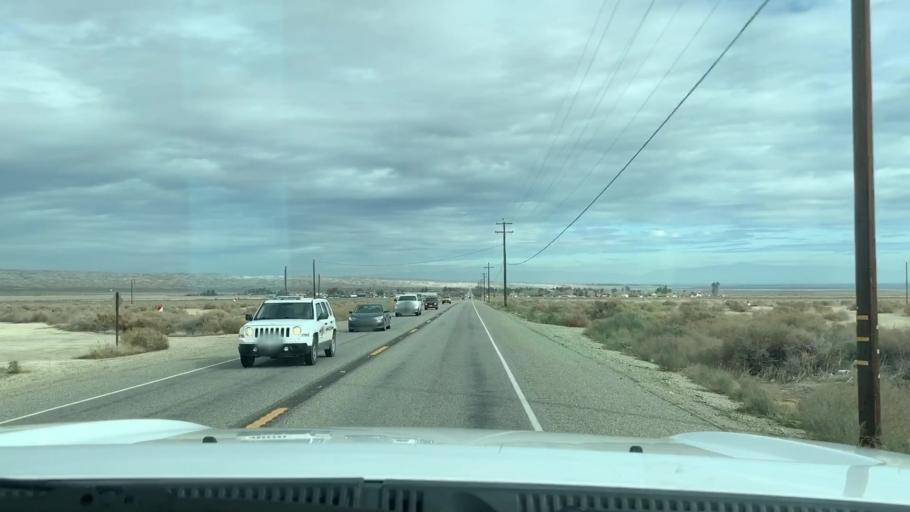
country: US
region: California
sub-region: Kern County
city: Ford City
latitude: 35.1973
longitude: -119.4236
